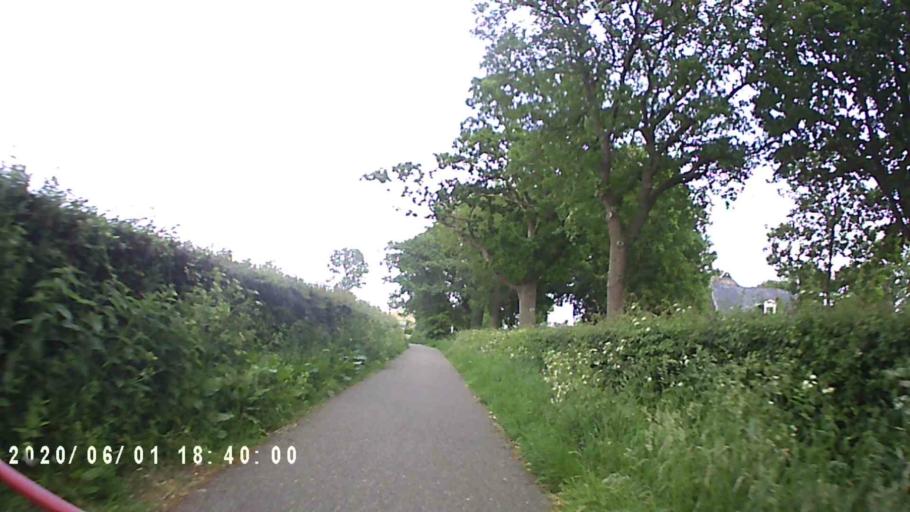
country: NL
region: Friesland
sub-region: Gemeente Tytsjerksteradiel
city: Eastermar
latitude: 53.1742
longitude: 6.0639
